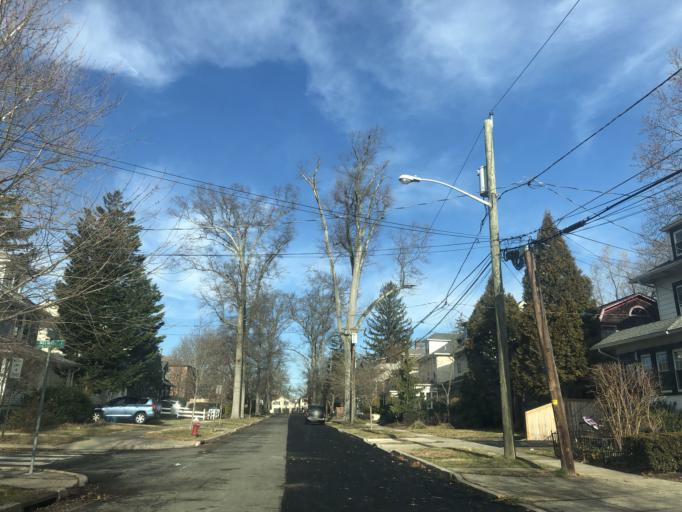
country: US
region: New Jersey
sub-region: Mercer County
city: Princeton
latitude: 40.3535
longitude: -74.6420
